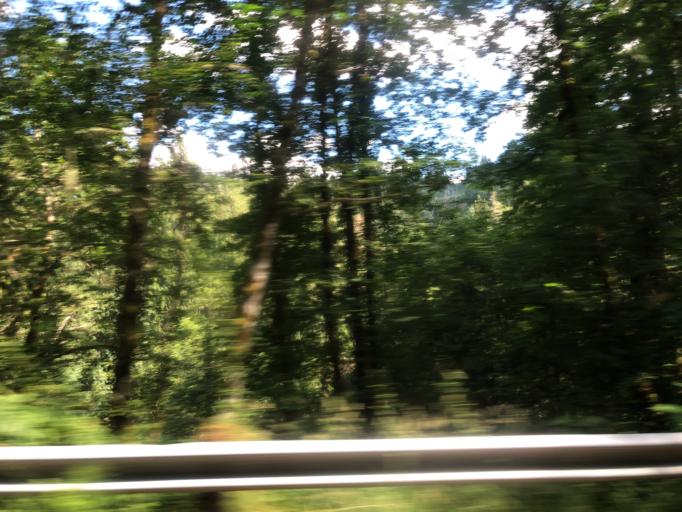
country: US
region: Oregon
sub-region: Clackamas County
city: Sandy
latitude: 45.4256
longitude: -122.2220
